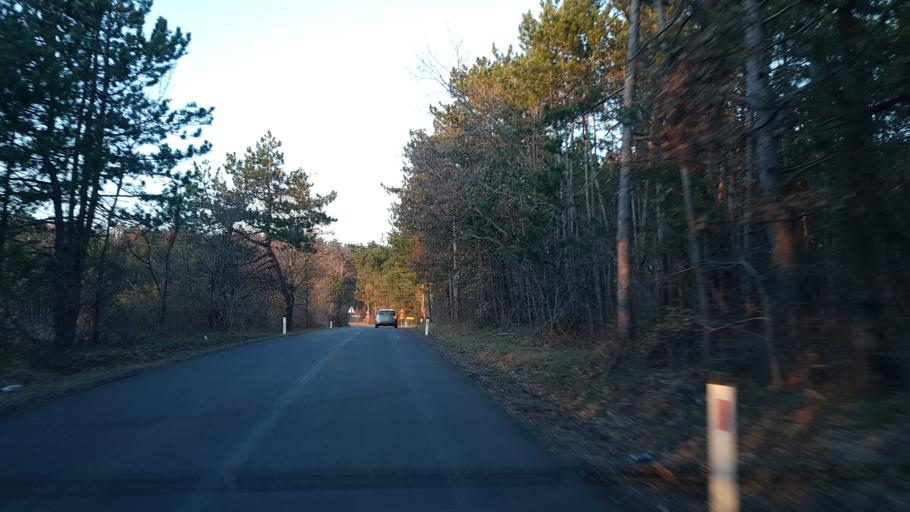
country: SI
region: Koper-Capodistria
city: Sv. Anton
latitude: 45.5168
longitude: 13.8597
